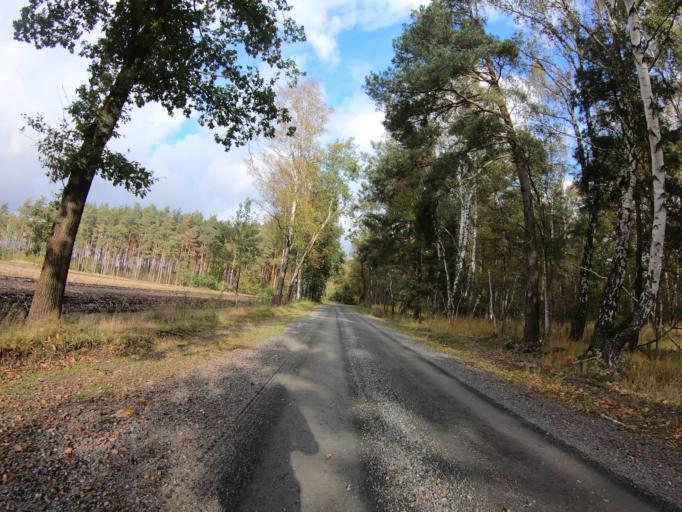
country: DE
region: Lower Saxony
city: Wesendorf
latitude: 52.5632
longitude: 10.5579
